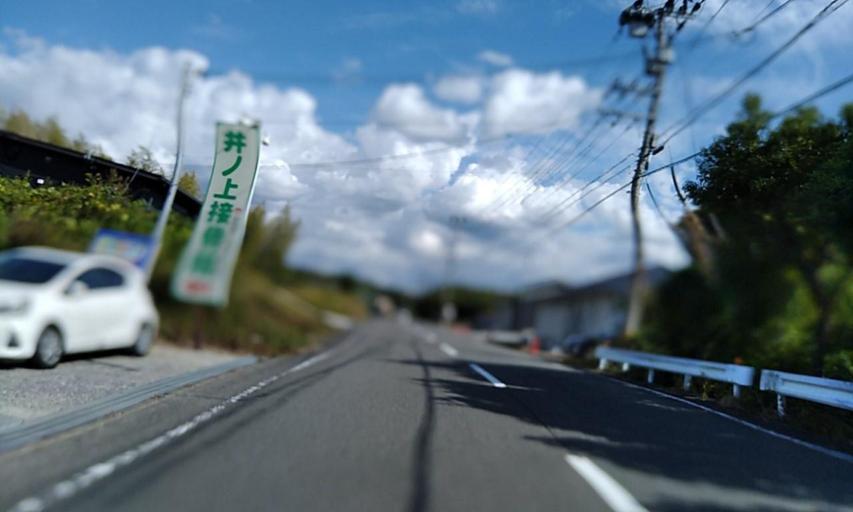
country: JP
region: Wakayama
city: Gobo
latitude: 33.8891
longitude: 135.1729
